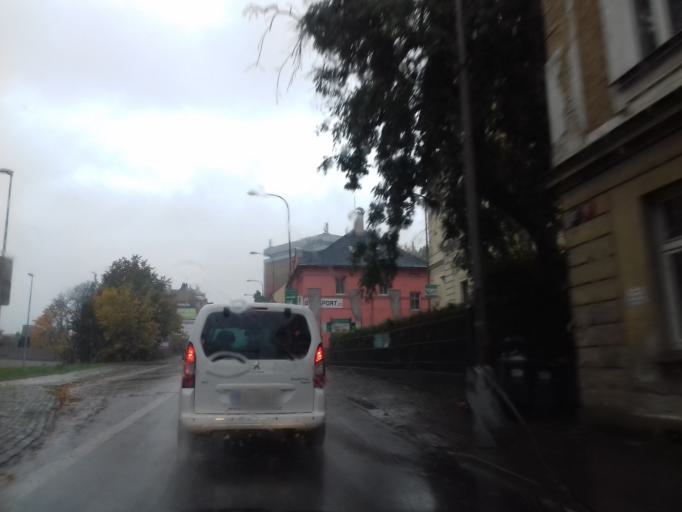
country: CZ
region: Liberecky
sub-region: Okres Liberec
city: Liberec
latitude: 50.7622
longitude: 15.0538
